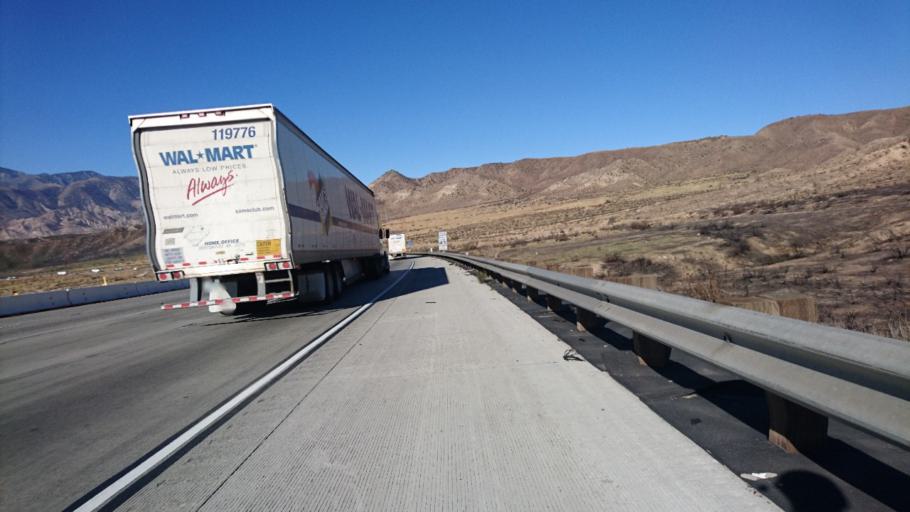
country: US
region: California
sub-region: San Bernardino County
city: Oak Hills
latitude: 34.3472
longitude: -117.4682
